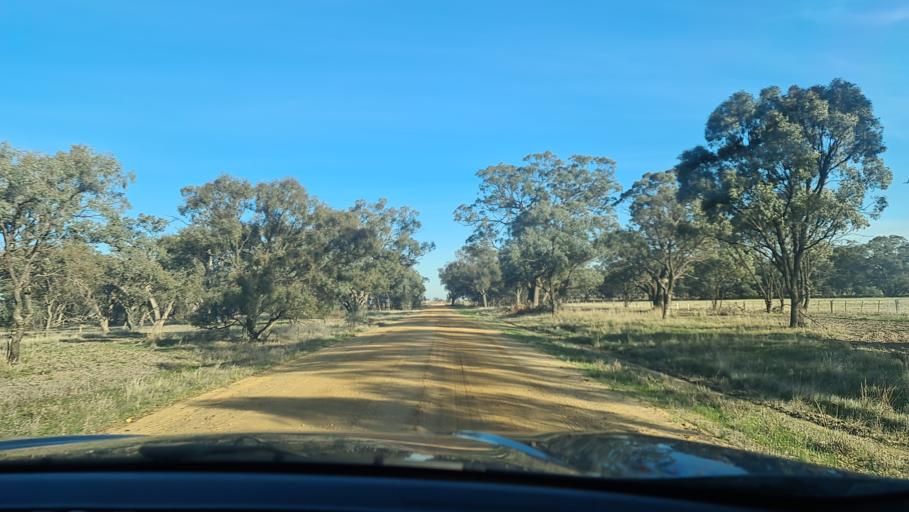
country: AU
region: Victoria
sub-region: Horsham
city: Horsham
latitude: -36.3538
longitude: 142.3985
